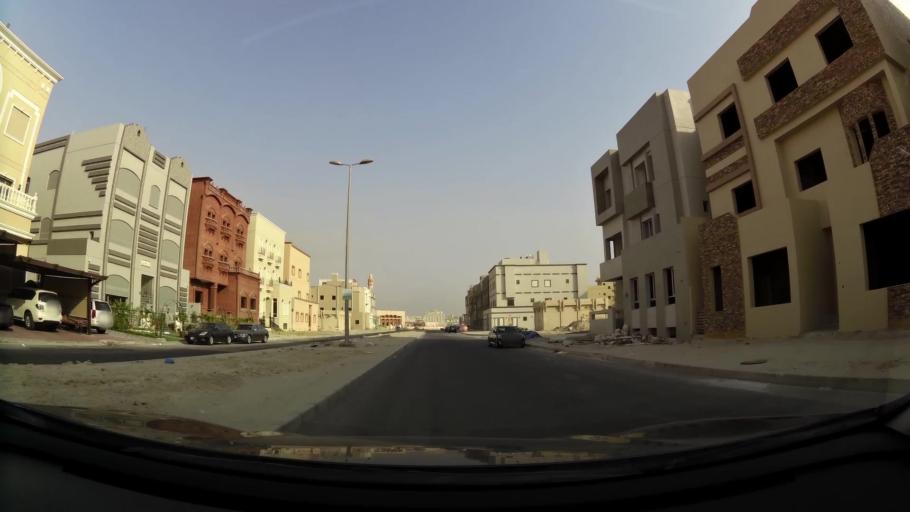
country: KW
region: Al Asimah
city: Ar Rabiyah
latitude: 29.3252
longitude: 47.8107
